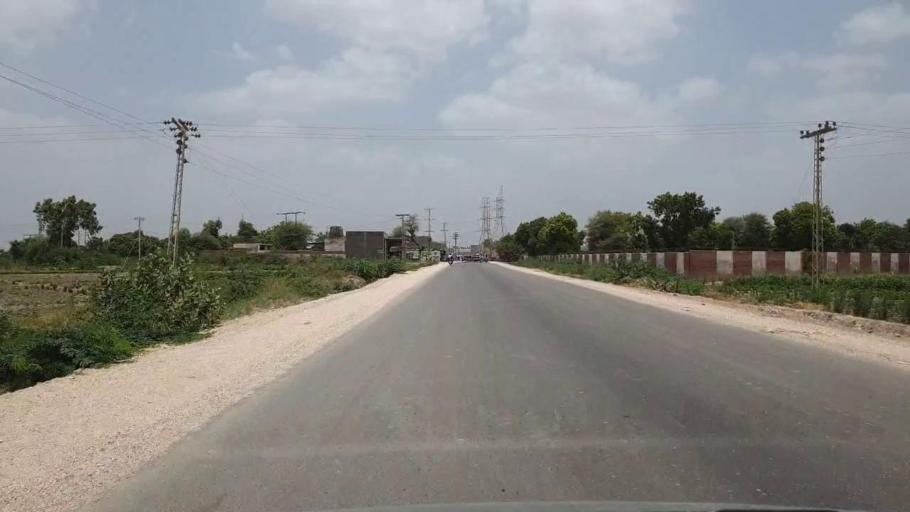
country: PK
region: Sindh
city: Naukot
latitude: 24.8506
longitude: 69.4099
